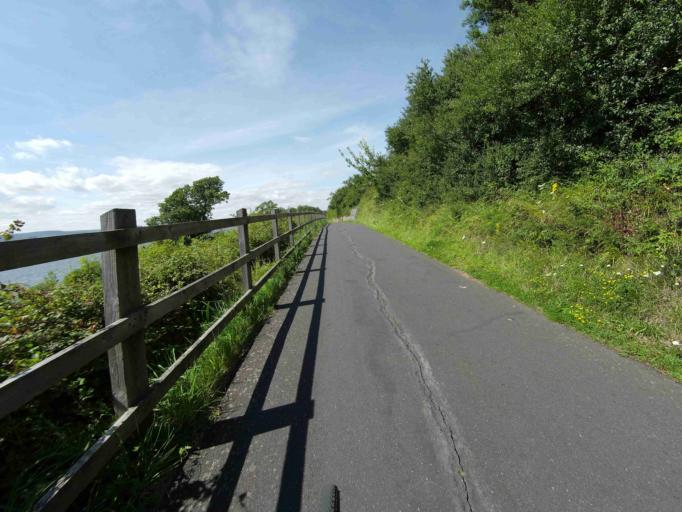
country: GB
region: England
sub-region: Devon
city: Starcross
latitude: 50.6414
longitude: -3.4255
